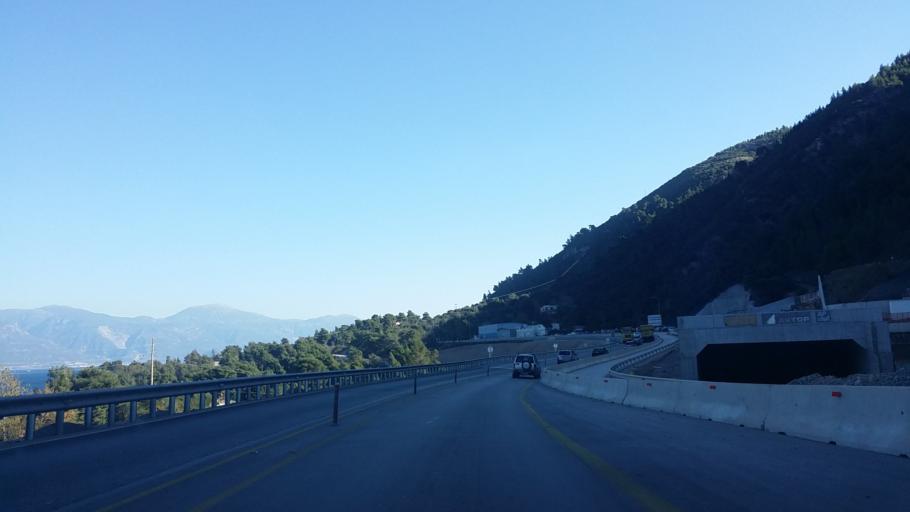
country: GR
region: West Greece
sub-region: Nomos Achaias
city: Kamarai
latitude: 38.3238
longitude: 21.9202
